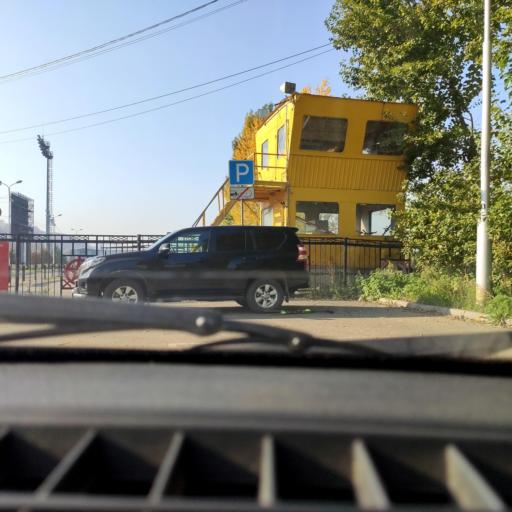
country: RU
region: Bashkortostan
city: Ufa
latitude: 54.8077
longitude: 56.0366
